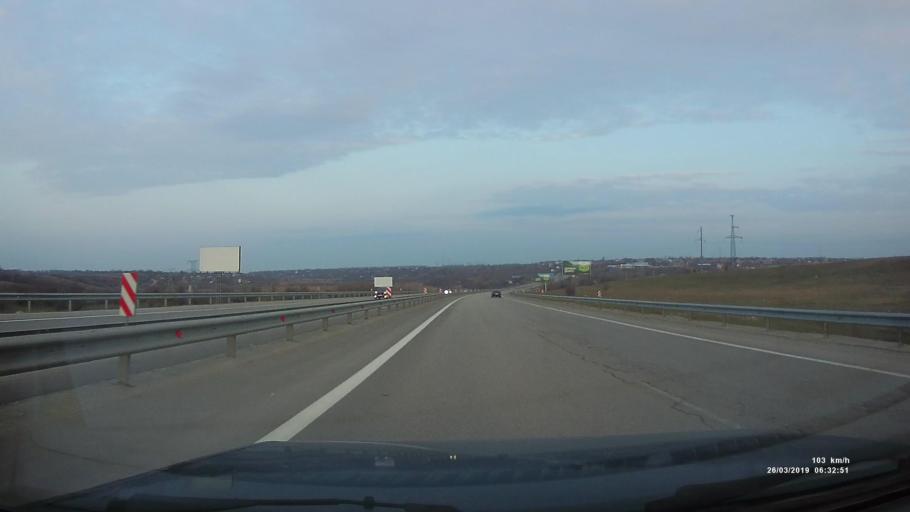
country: RU
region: Rostov
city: Chaltyr
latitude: 47.2698
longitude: 39.5018
